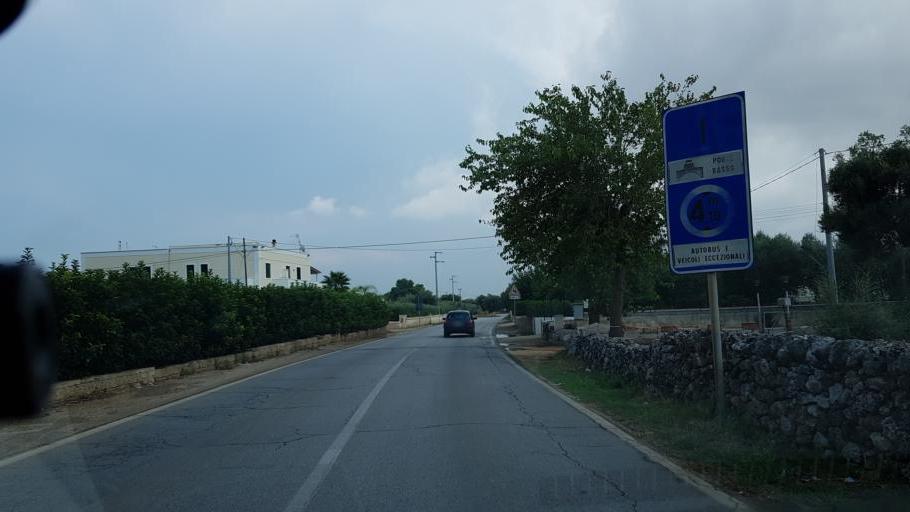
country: IT
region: Apulia
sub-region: Provincia di Brindisi
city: Fasano
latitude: 40.8530
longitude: 17.3855
